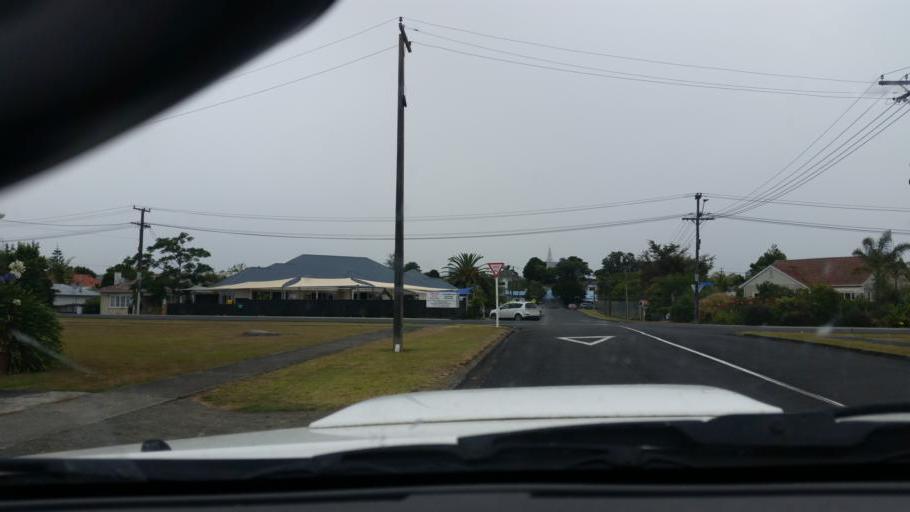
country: NZ
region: Northland
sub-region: Kaipara District
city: Dargaville
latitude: -35.9370
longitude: 173.8679
